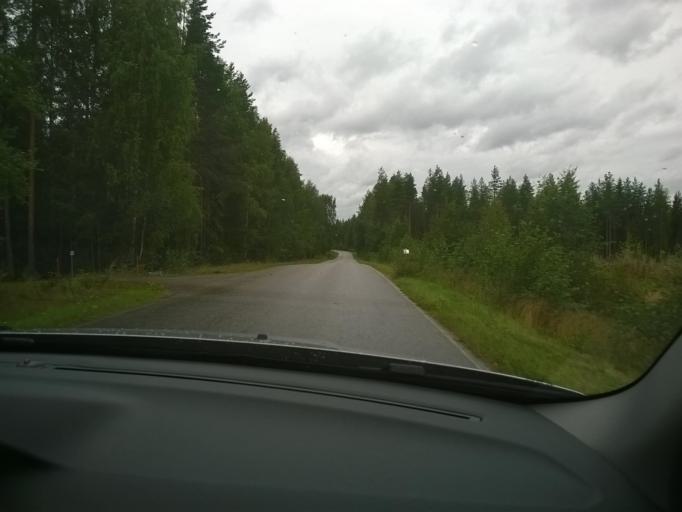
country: FI
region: Kainuu
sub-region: Kehys-Kainuu
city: Kuhmo
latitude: 64.1361
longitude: 29.4250
